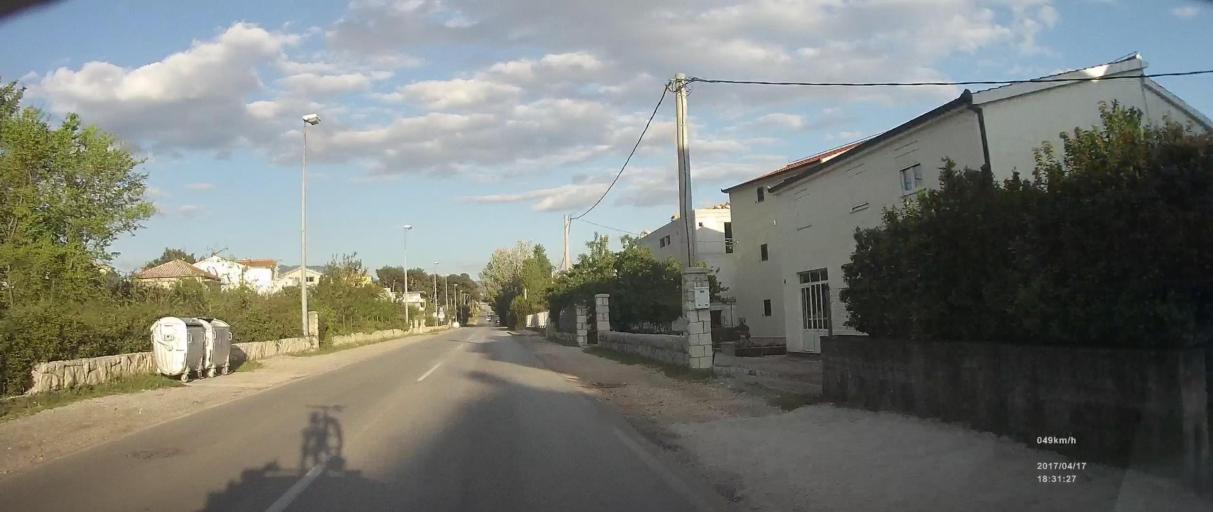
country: HR
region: Splitsko-Dalmatinska
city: Vranjic
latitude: 43.5450
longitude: 16.4344
